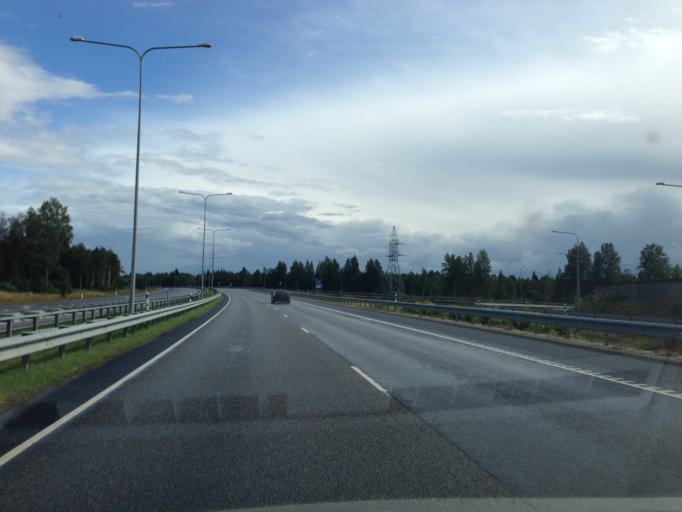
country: EE
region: Jaervamaa
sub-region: Paide linn
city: Paide
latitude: 58.9024
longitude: 25.6363
